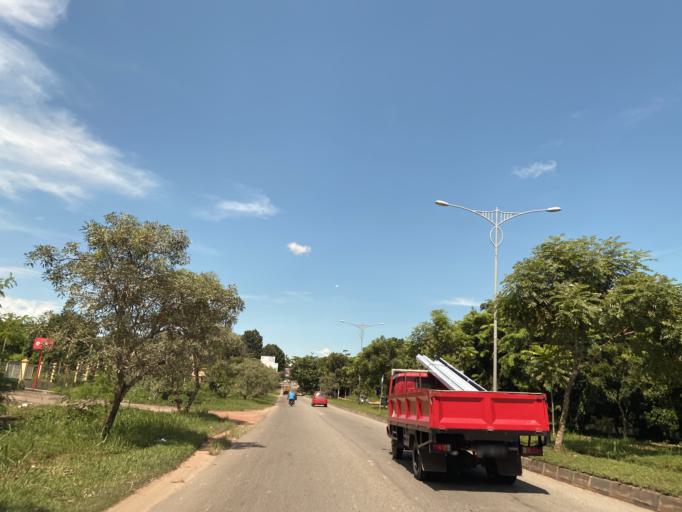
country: SG
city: Singapore
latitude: 1.1093
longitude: 104.0606
